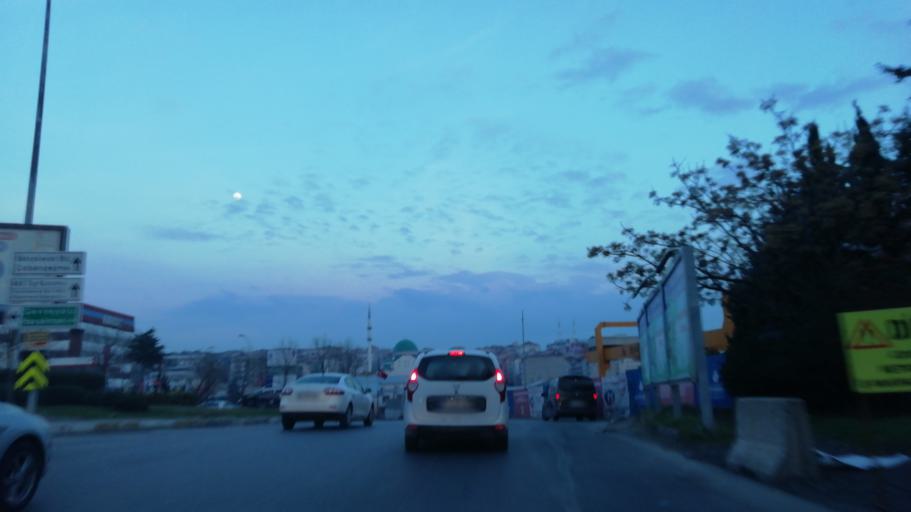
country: TR
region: Istanbul
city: Bahcelievler
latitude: 41.0005
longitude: 28.8216
